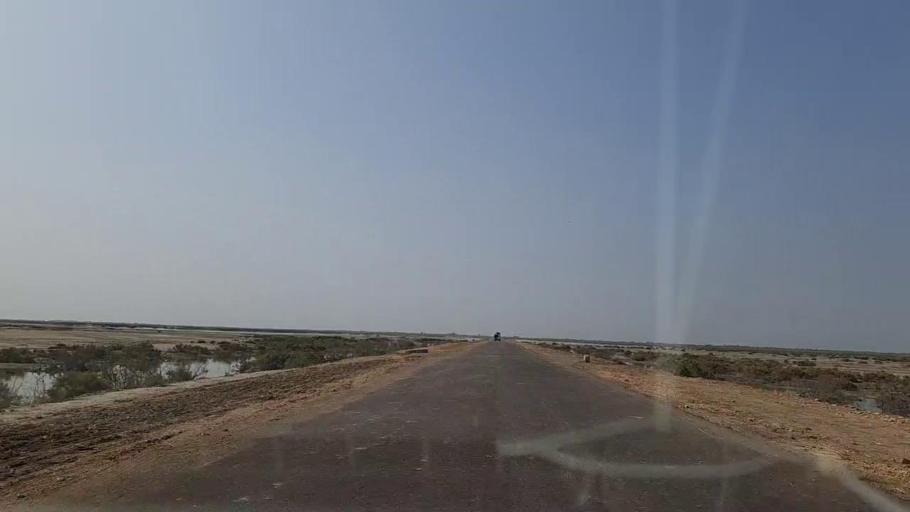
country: PK
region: Sindh
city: Chuhar Jamali
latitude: 24.2227
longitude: 67.8913
